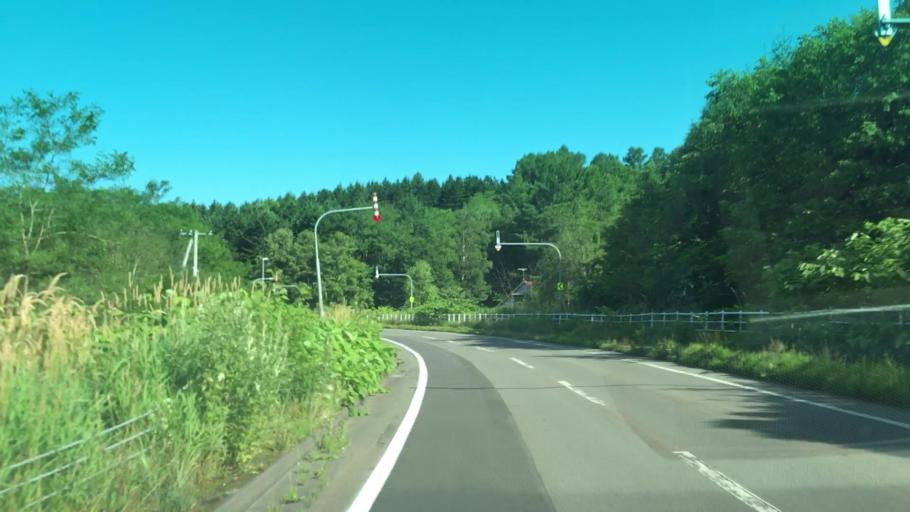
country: JP
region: Hokkaido
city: Yoichi
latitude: 43.0651
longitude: 140.7073
